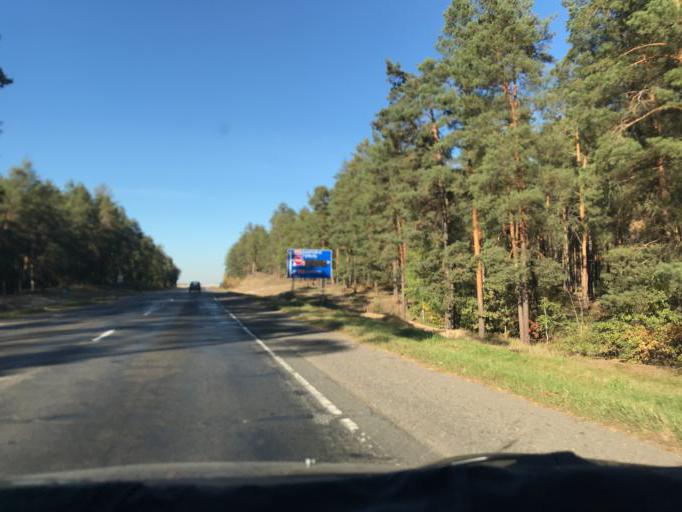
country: BY
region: Gomel
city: Kalinkavichy
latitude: 52.0658
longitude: 29.3611
